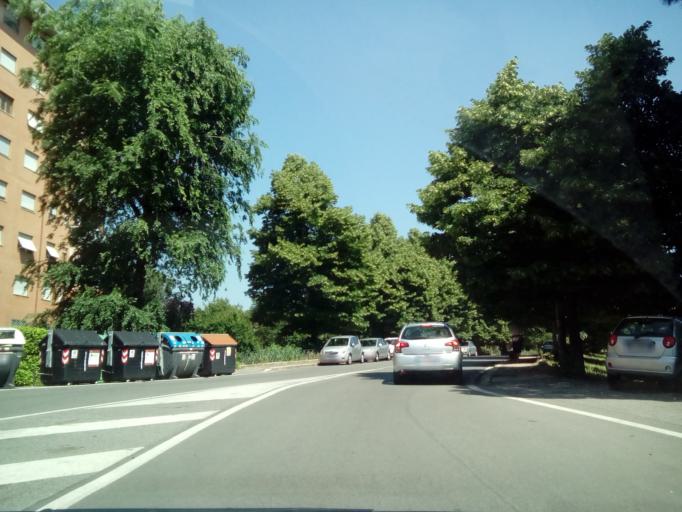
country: IT
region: Latium
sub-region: Citta metropolitana di Roma Capitale
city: Rome
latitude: 41.8835
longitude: 12.5892
